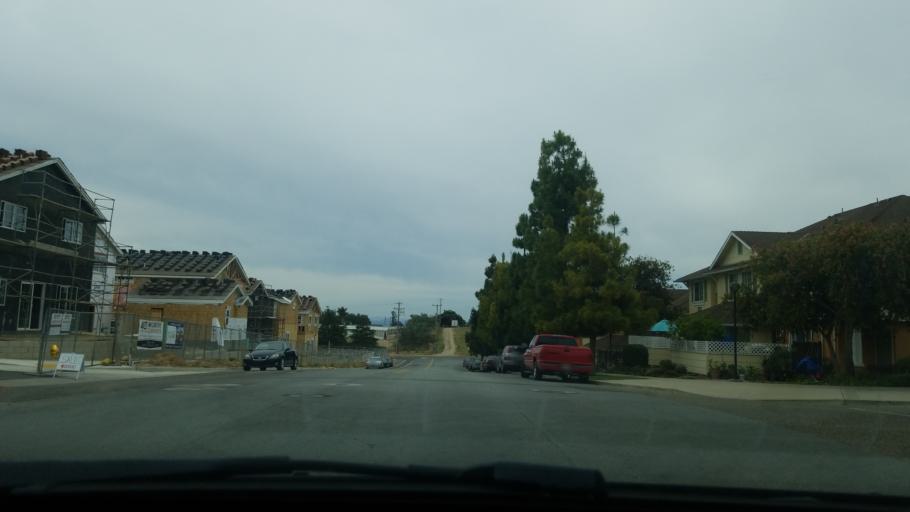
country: US
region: California
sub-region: San Luis Obispo County
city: Nipomo
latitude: 35.0311
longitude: -120.4865
